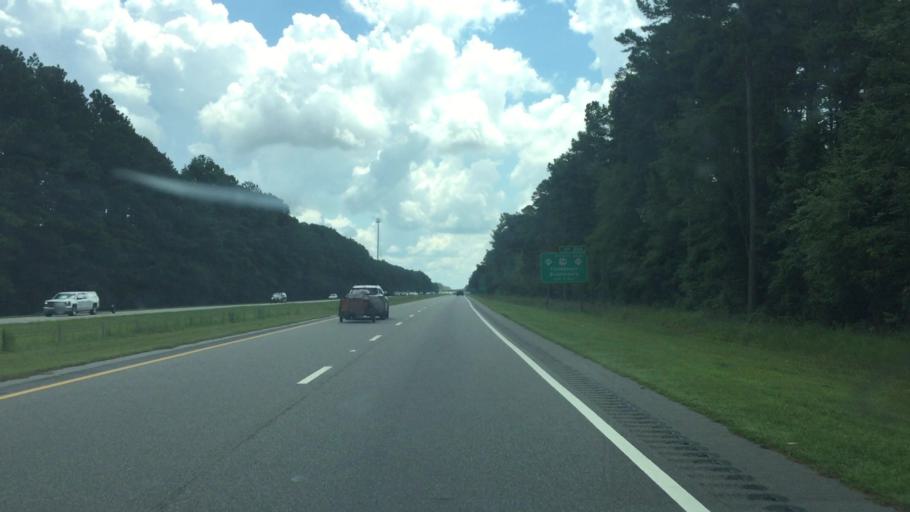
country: US
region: North Carolina
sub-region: Columbus County
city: Chadbourn
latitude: 34.3745
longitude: -78.8458
